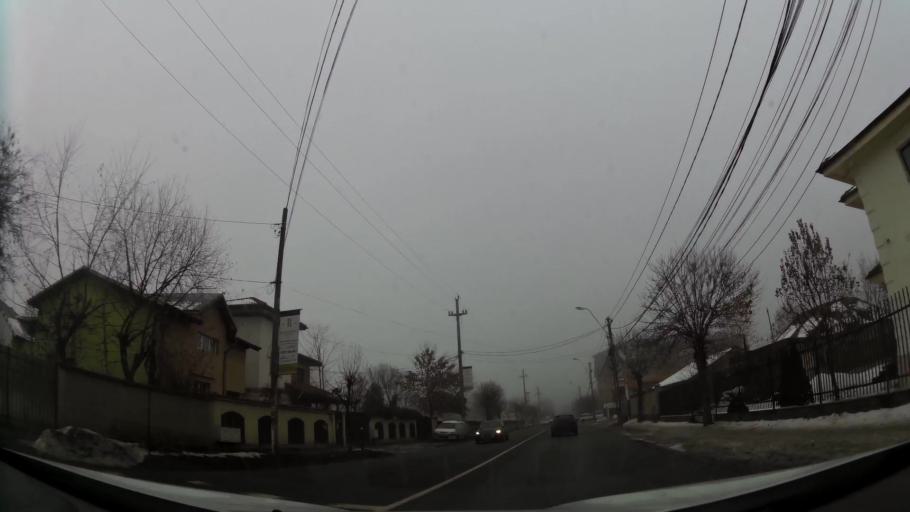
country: RO
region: Ilfov
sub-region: Comuna Chiajna
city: Rosu
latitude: 44.4475
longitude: 26.0153
